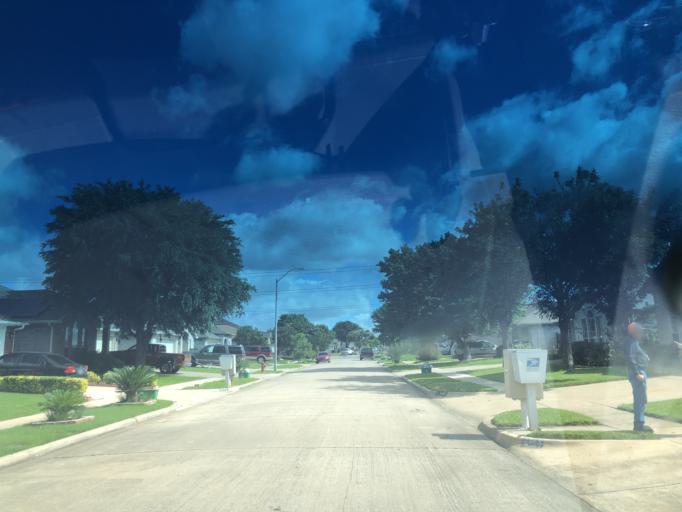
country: US
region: Texas
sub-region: Dallas County
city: Grand Prairie
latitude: 32.6969
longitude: -97.0291
